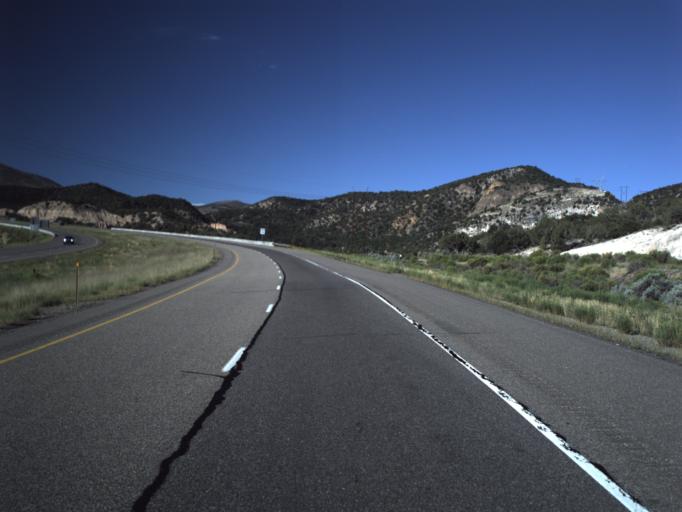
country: US
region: Utah
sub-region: Sevier County
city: Monroe
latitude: 38.5644
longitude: -112.3578
